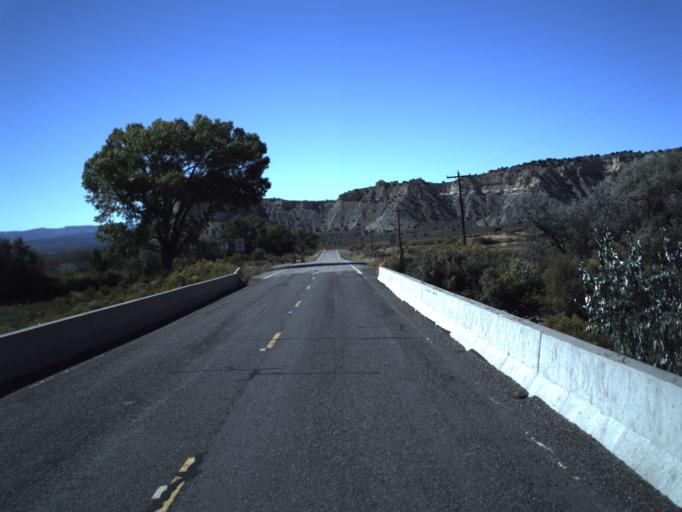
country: US
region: Utah
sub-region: Garfield County
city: Panguitch
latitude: 37.5626
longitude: -112.0004
